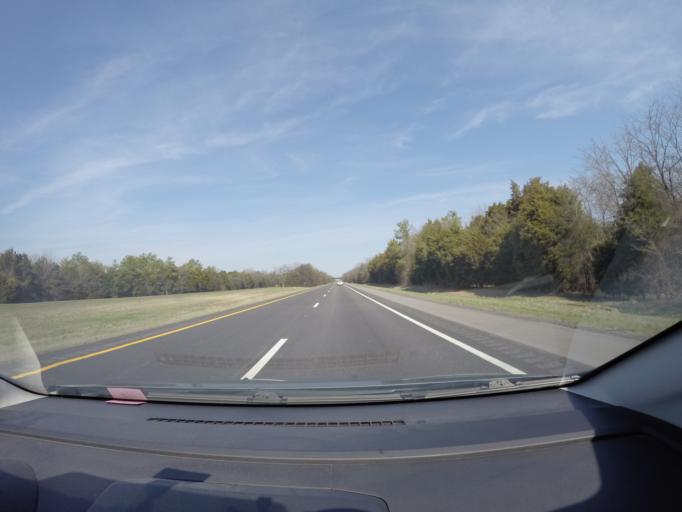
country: US
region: Tennessee
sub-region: Rutherford County
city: Plainview
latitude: 35.6993
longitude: -86.3026
